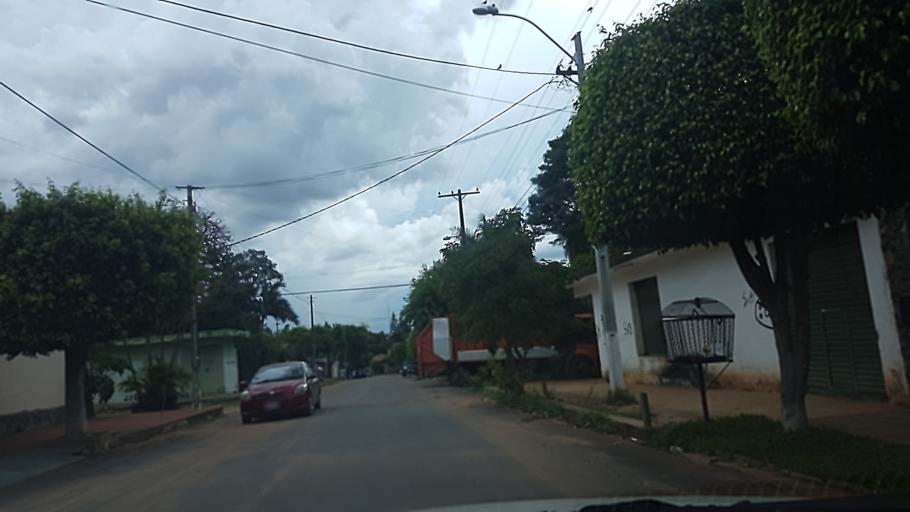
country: PY
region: Central
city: Colonia Mariano Roque Alonso
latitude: -25.2130
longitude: -57.5264
